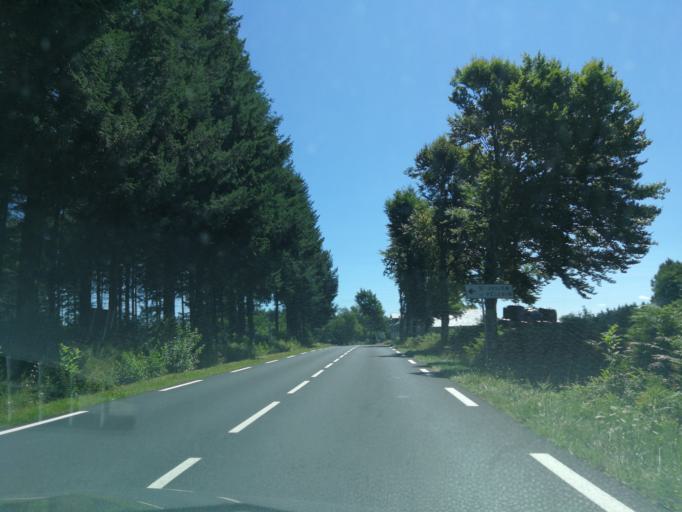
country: FR
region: Auvergne
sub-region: Departement du Cantal
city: Laroquebrou
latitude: 45.0014
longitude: 2.0551
